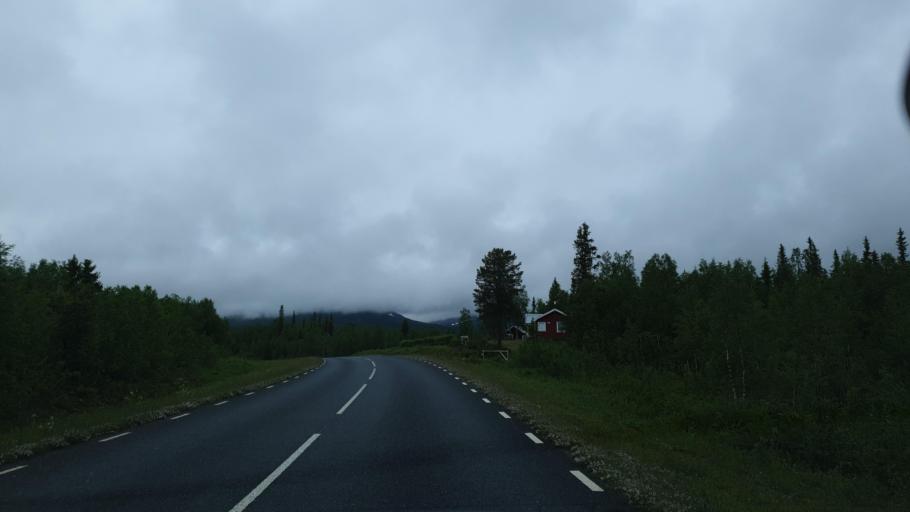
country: SE
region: Vaesterbotten
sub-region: Vilhelmina Kommun
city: Sjoberg
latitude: 65.2556
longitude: 15.7214
